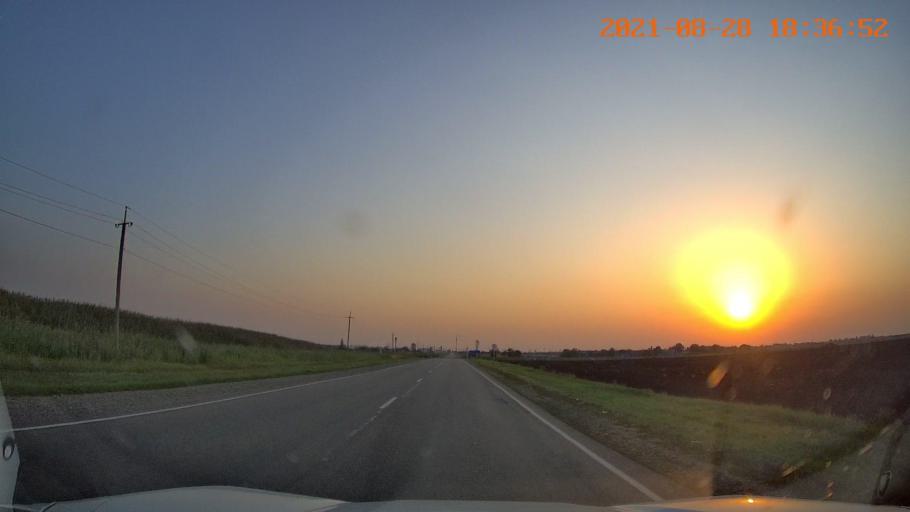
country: RU
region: Adygeya
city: Giaginskaya
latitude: 44.8637
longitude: 40.1020
